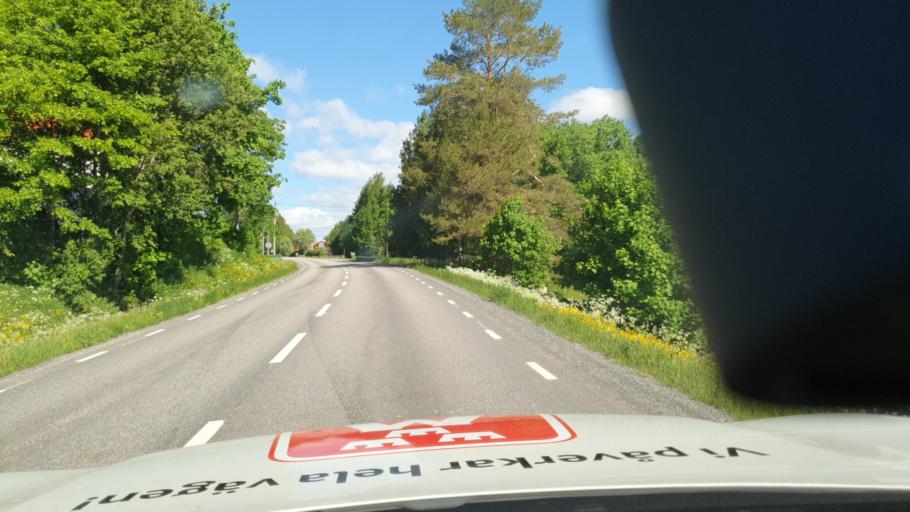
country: SE
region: Vaesterbotten
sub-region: Vannas Kommun
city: Vaennaes
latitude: 63.7830
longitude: 19.8405
